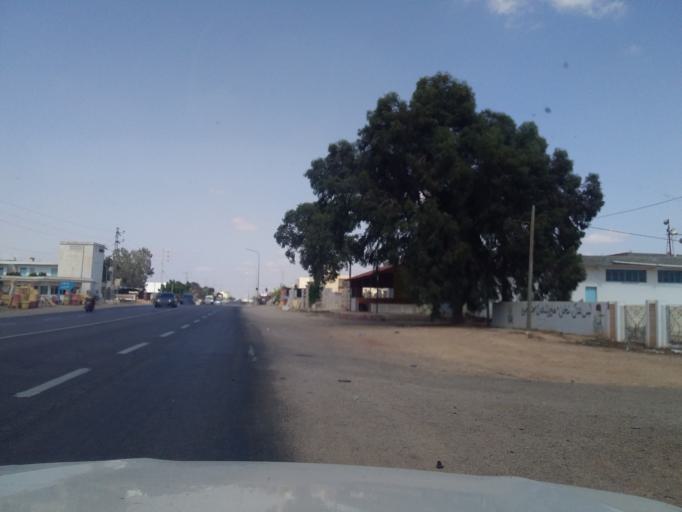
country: TN
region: Madanin
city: Medenine
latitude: 33.6033
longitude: 10.3052
